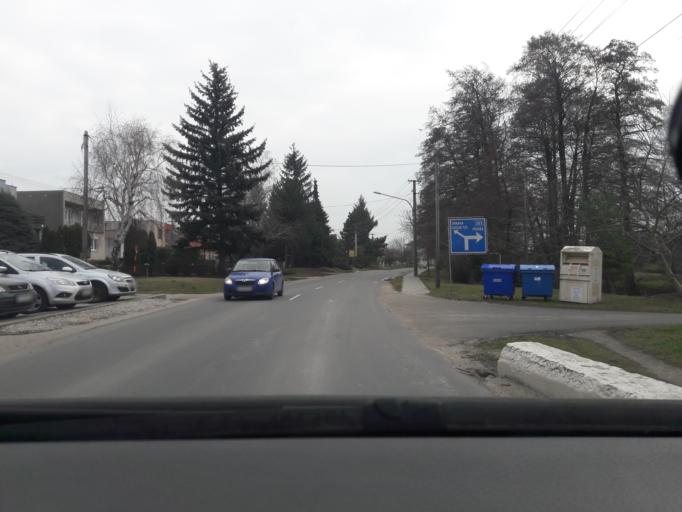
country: SK
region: Trnavsky
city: Smolenice
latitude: 48.4688
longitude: 17.4406
